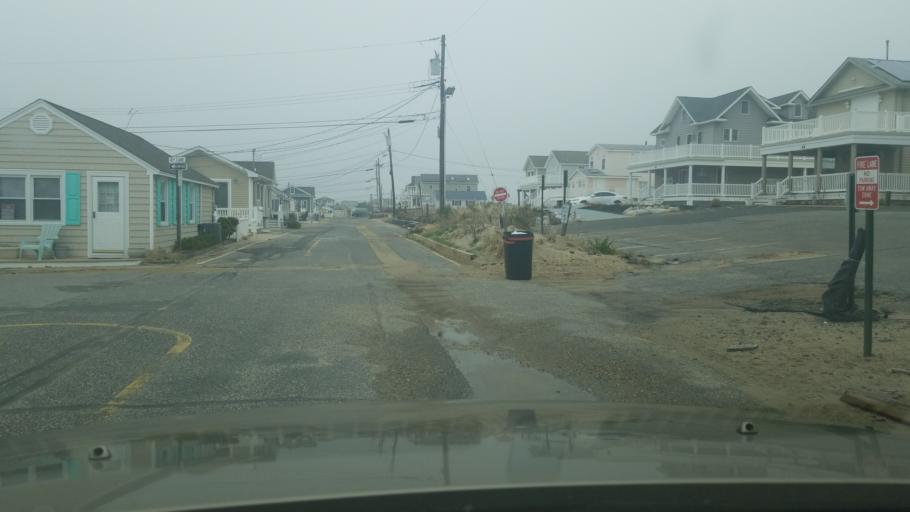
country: US
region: New Jersey
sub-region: Ocean County
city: Seaside Park
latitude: 39.9097
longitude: -74.0788
